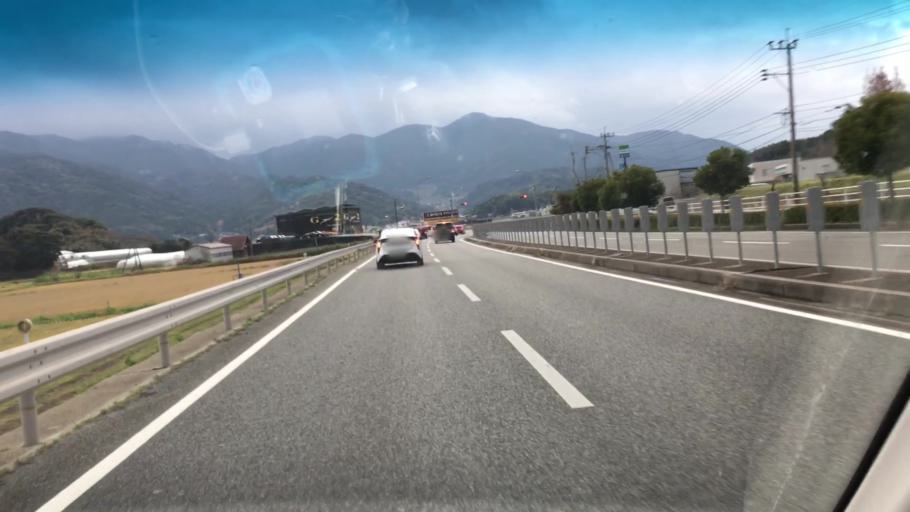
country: JP
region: Fukuoka
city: Maebaru-chuo
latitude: 33.5261
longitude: 130.1748
